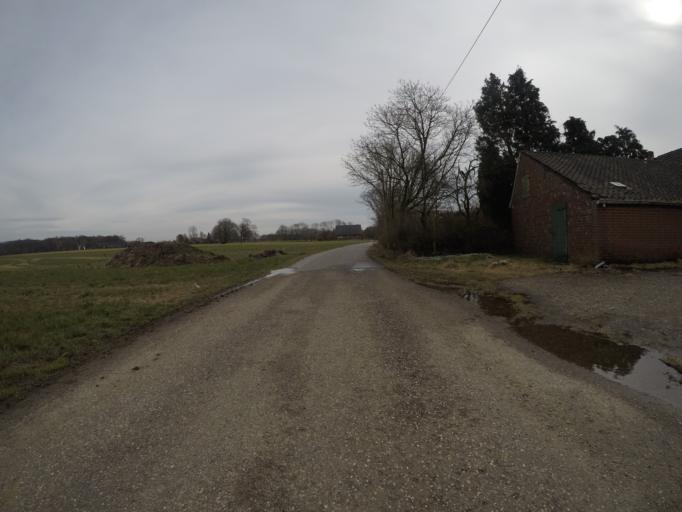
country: DE
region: North Rhine-Westphalia
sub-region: Regierungsbezirk Dusseldorf
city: Mehrhoog
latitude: 51.7837
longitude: 6.5504
